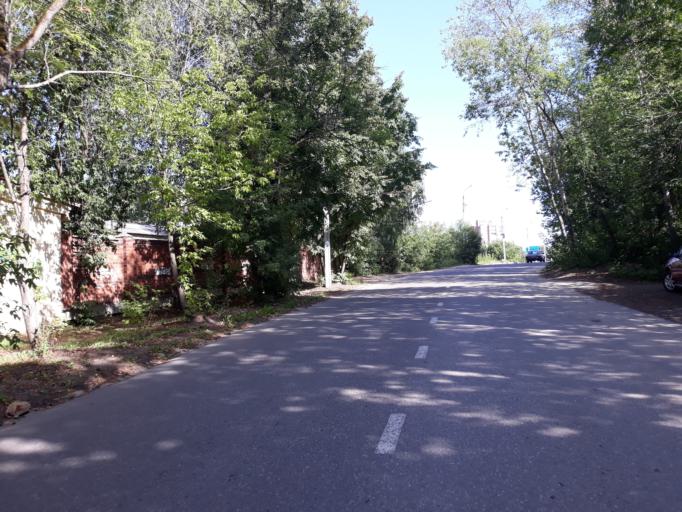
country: RU
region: Jaroslavl
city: Yaroslavl
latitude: 57.5953
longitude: 39.8588
